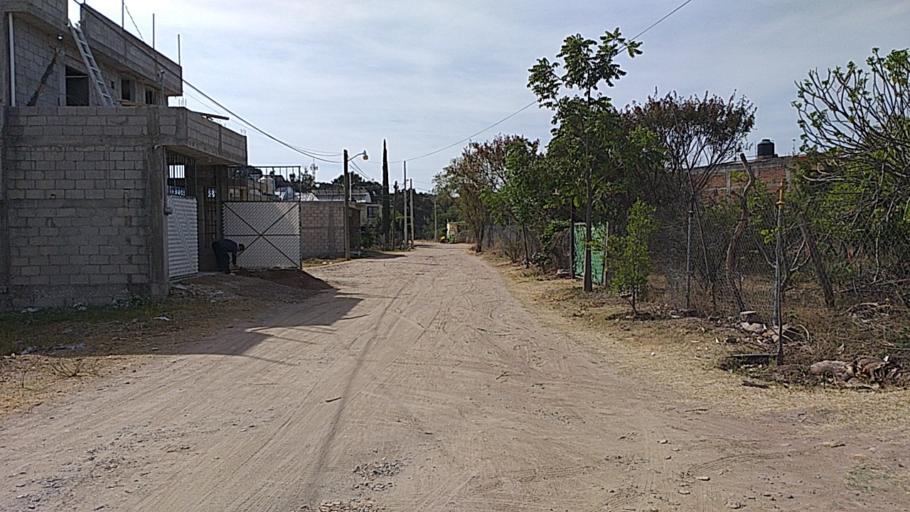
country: MX
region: Oaxaca
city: Ciudad de Huajuapam de Leon
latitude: 17.8113
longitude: -97.7672
